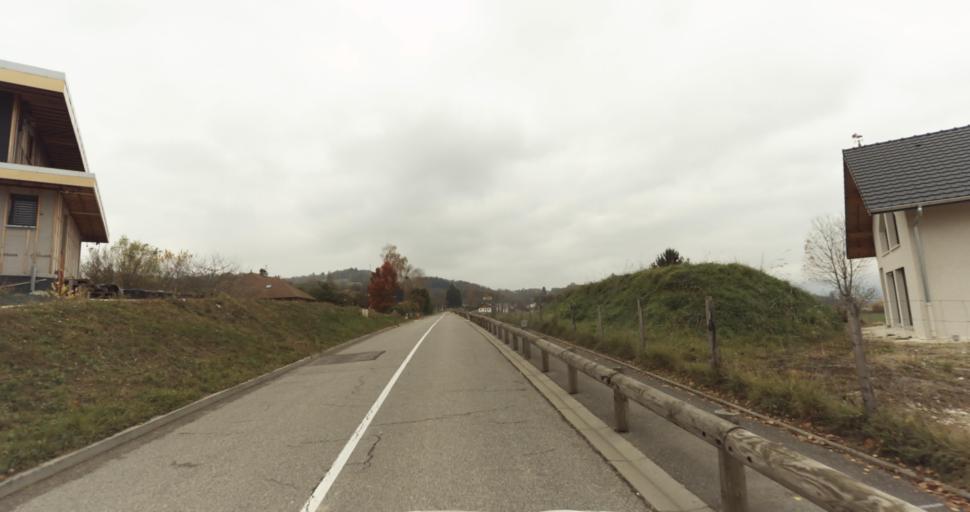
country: FR
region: Rhone-Alpes
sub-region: Departement de la Haute-Savoie
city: Alby-sur-Cheran
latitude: 45.8145
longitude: 6.0116
